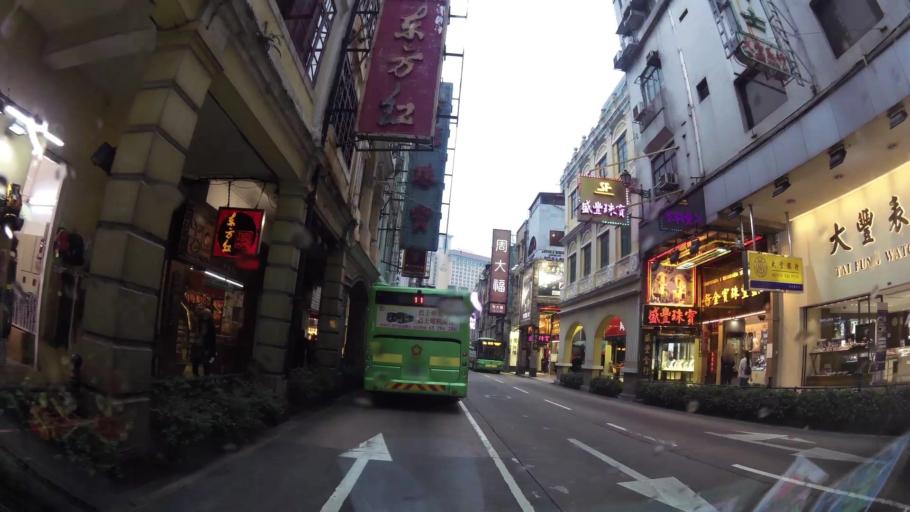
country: MO
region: Macau
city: Macau
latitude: 22.1943
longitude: 113.5387
